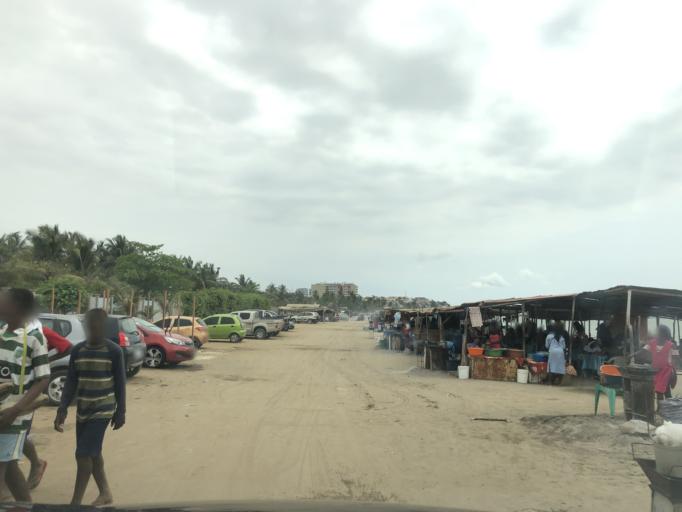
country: AO
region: Luanda
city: Luanda
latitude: -8.8720
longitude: 13.1939
